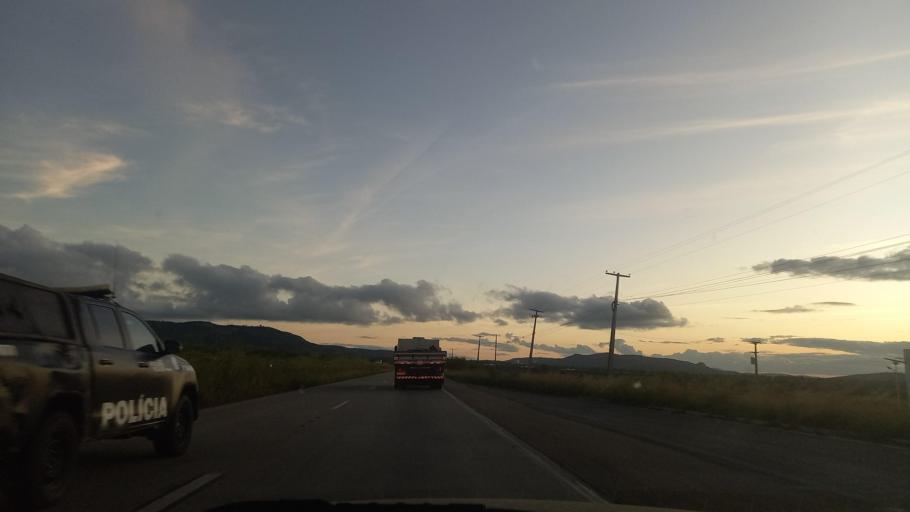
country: BR
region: Pernambuco
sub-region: Bezerros
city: Bezerros
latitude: -8.2773
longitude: -35.8075
